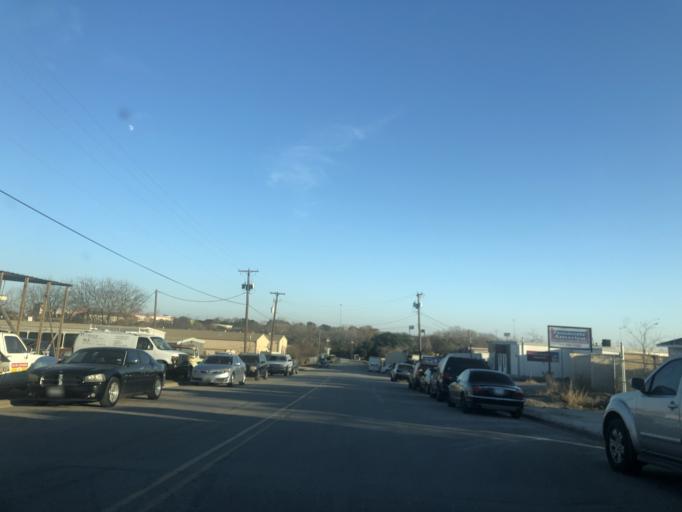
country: US
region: Texas
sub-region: Travis County
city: Wells Branch
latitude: 30.4297
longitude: -97.6786
